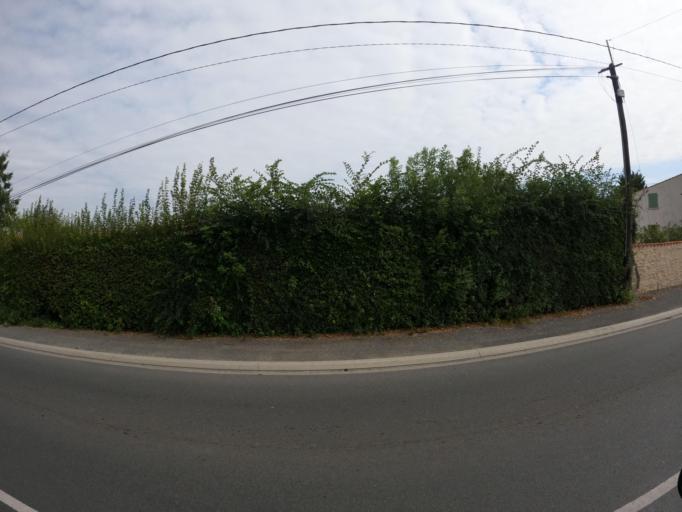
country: FR
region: Poitou-Charentes
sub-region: Departement de la Charente-Maritime
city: Saint-Jean-de-Liversay
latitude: 46.2681
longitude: -0.8827
